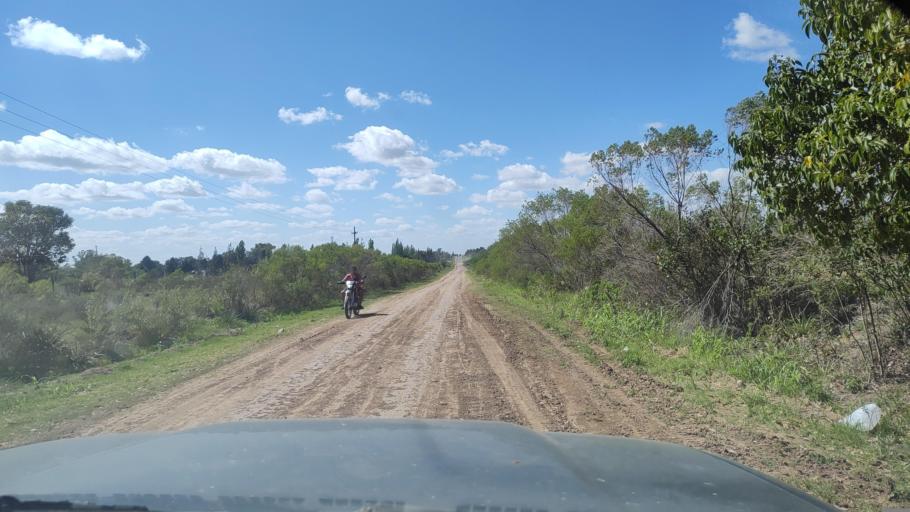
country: AR
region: Buenos Aires
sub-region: Partido de Lujan
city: Lujan
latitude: -34.5366
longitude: -59.1463
